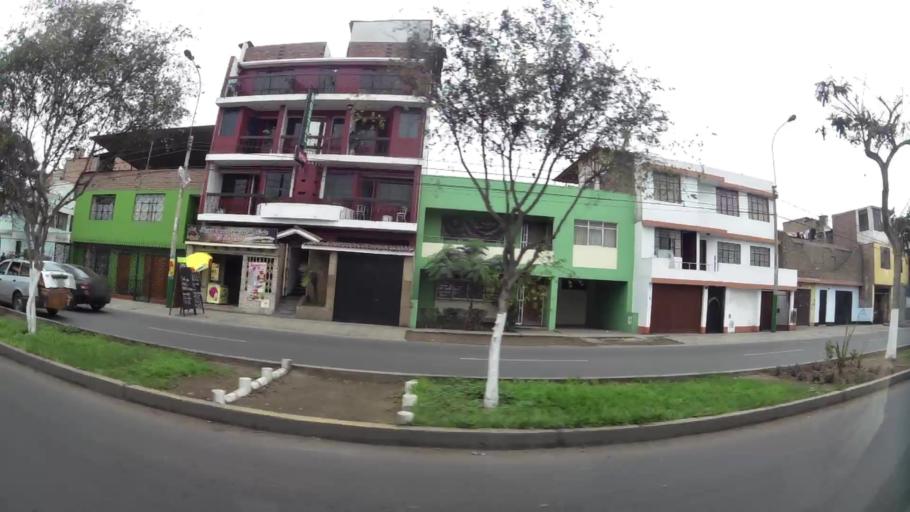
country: PE
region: Lima
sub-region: Lima
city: Surco
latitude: -12.1600
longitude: -76.9692
